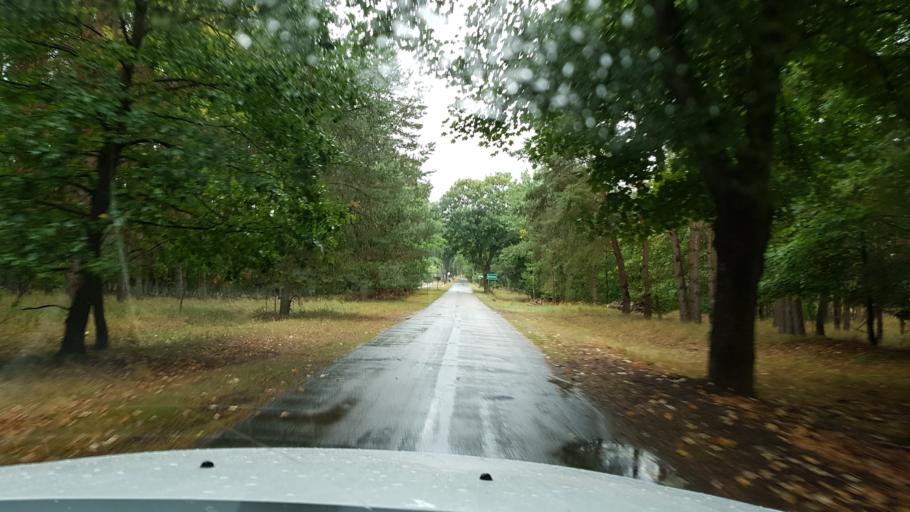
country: DE
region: Brandenburg
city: Schoneberg
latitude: 52.9459
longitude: 14.1570
